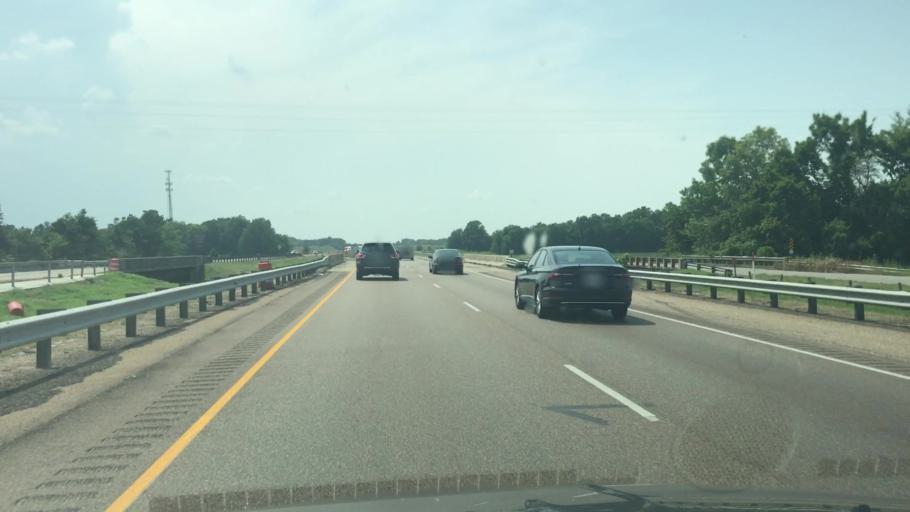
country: US
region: Arkansas
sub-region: Crittenden County
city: Earle
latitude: 35.1495
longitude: -90.3545
